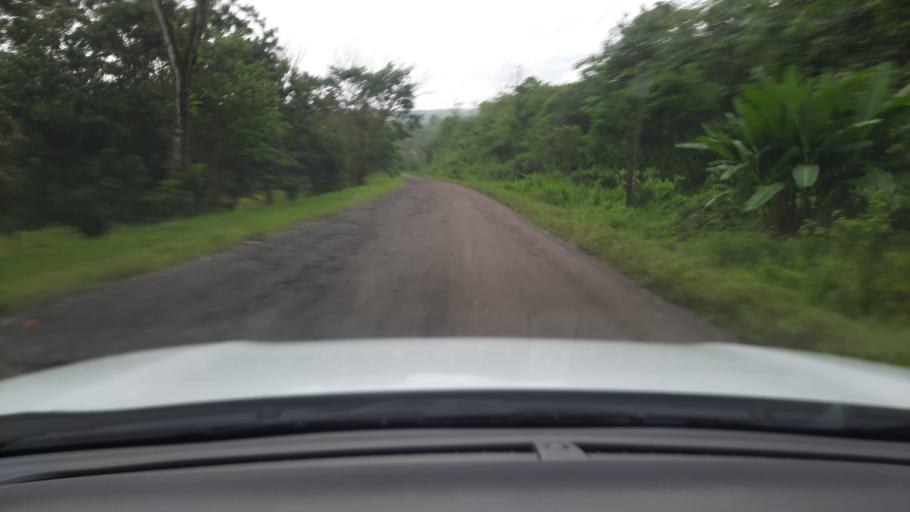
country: CR
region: Alajuela
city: San Jose
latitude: 11.0001
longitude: -85.2875
